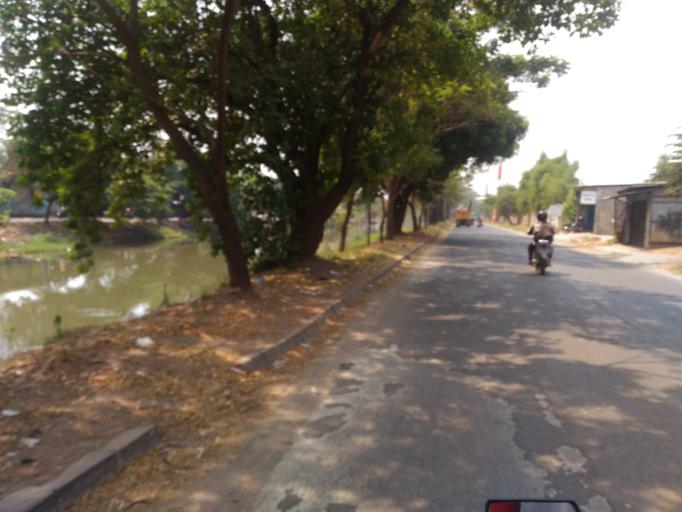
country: ID
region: West Java
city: Sepatan
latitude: -6.1485
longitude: 106.5929
